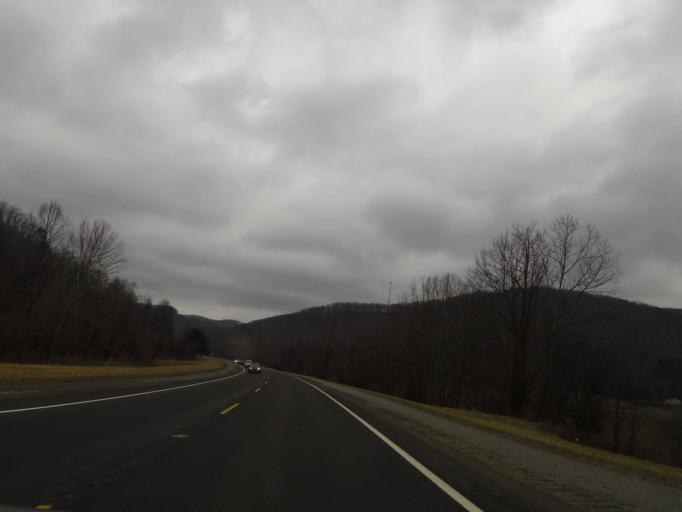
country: US
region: Tennessee
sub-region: Scott County
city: Huntsville
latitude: 36.3811
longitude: -84.3470
